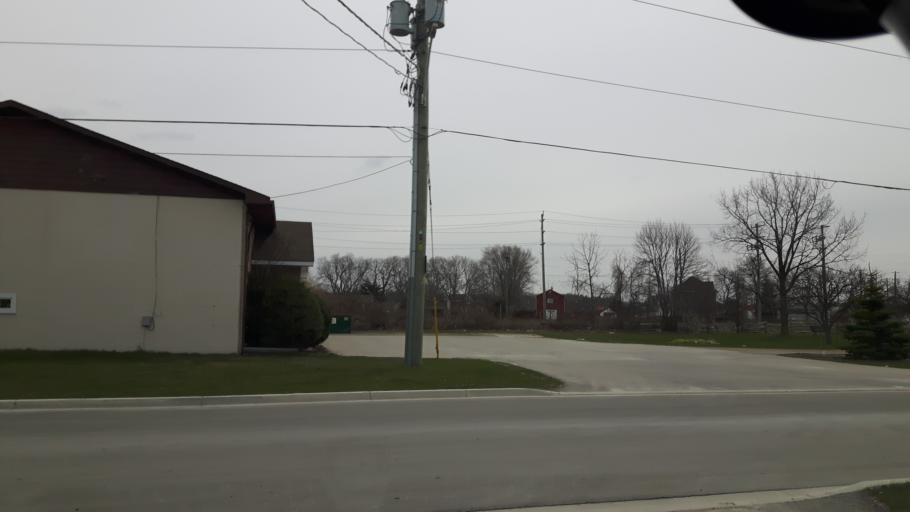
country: CA
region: Ontario
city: Goderich
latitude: 43.7331
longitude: -81.6927
